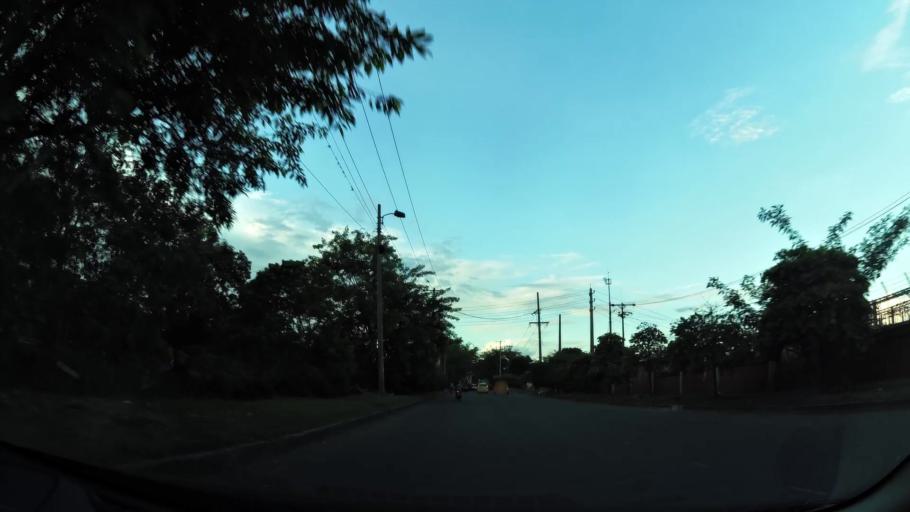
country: CO
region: Valle del Cauca
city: Cali
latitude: 3.4418
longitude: -76.4839
